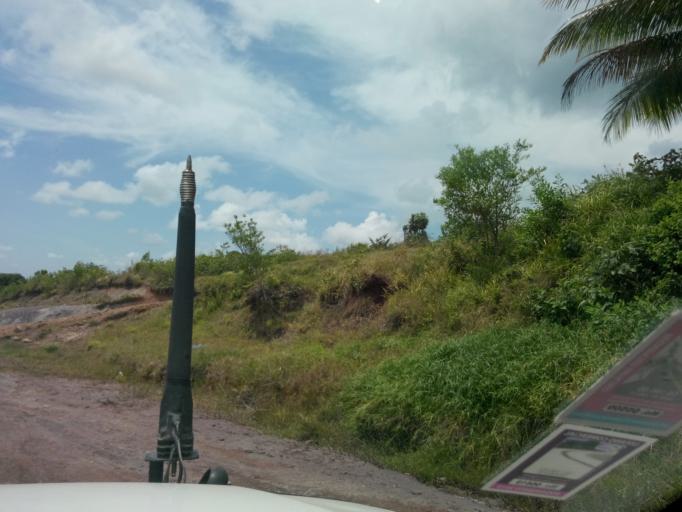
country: NI
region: Atlantico Sur
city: Bluefields
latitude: 12.0104
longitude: -83.7746
